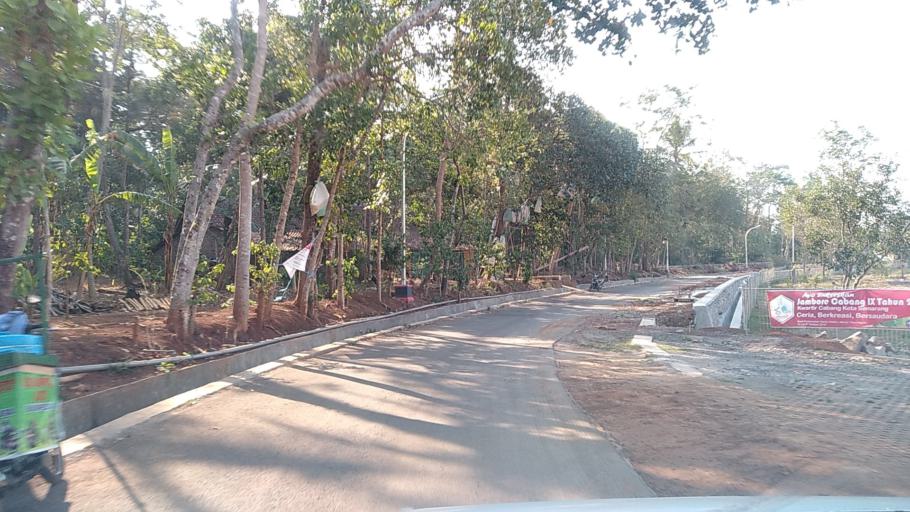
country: ID
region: Central Java
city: Ungaran
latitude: -7.0647
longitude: 110.3465
